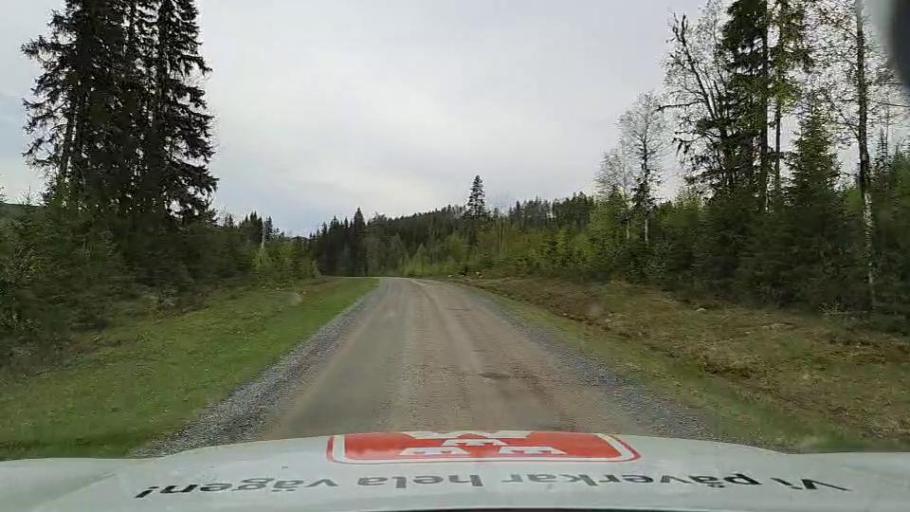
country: SE
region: Jaemtland
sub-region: Bergs Kommun
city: Hoverberg
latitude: 62.5364
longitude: 14.7021
